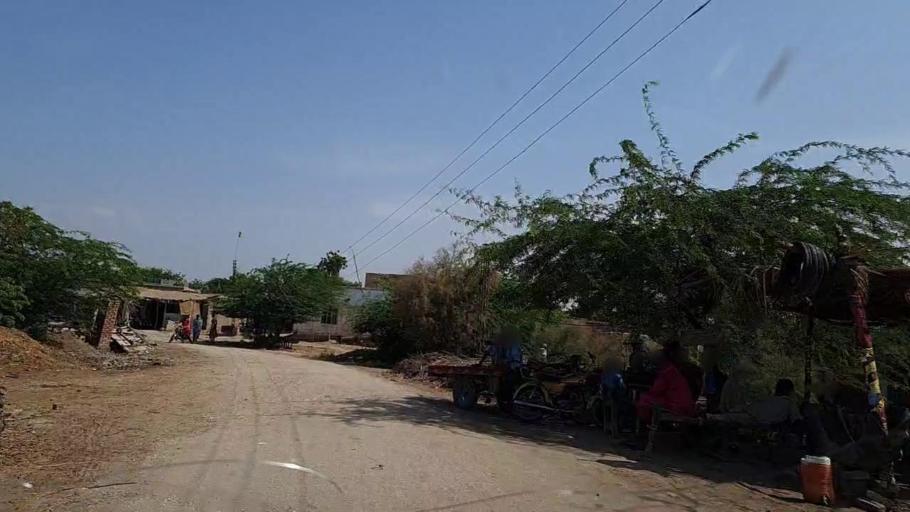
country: PK
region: Sindh
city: Khanpur
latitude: 27.7502
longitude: 69.3379
